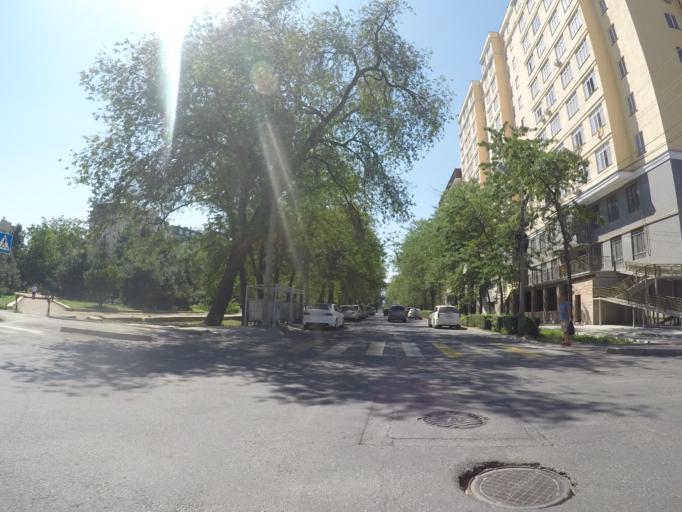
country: KG
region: Chuy
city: Bishkek
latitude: 42.8791
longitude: 74.5919
